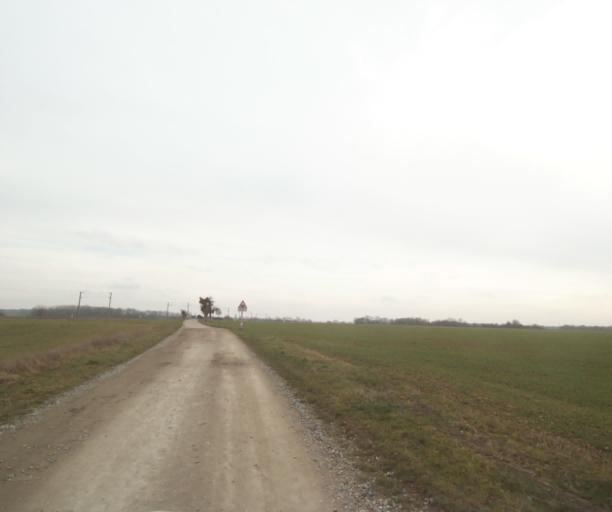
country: FR
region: Champagne-Ardenne
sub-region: Departement de la Haute-Marne
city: Villiers-en-Lieu
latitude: 48.6738
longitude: 4.8752
